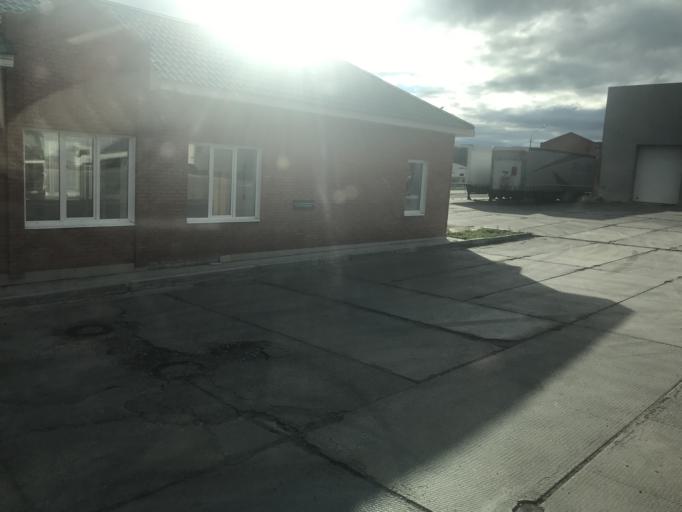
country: MN
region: Selenge
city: Altanbulag
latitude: 50.3262
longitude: 106.4861
